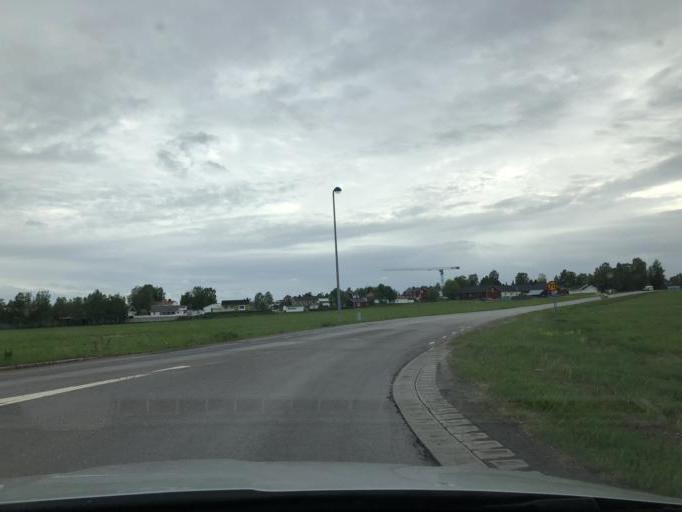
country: SE
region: Norrbotten
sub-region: Pitea Kommun
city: Bergsviken
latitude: 65.3522
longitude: 21.4017
